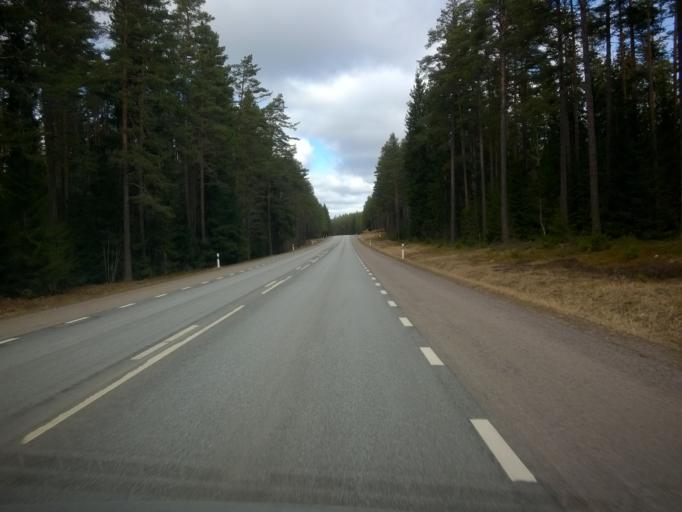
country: SE
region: Uppsala
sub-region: Tierps Kommun
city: Tierp
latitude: 60.2012
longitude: 17.4819
